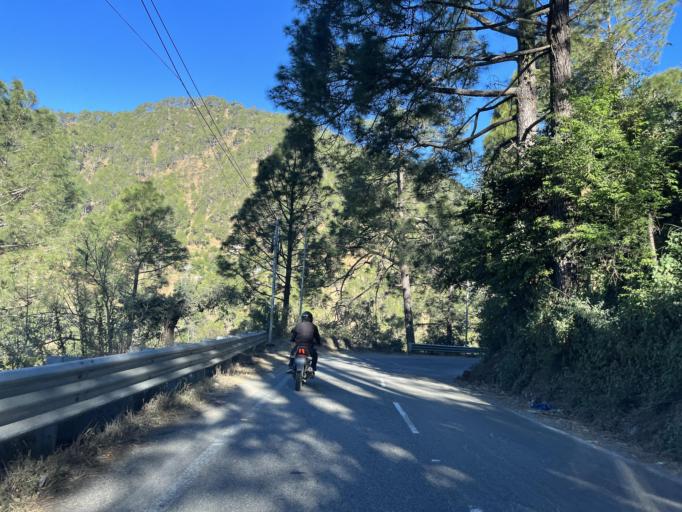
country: IN
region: Uttarakhand
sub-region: Naini Tal
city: Bhowali
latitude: 29.4072
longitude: 79.5143
